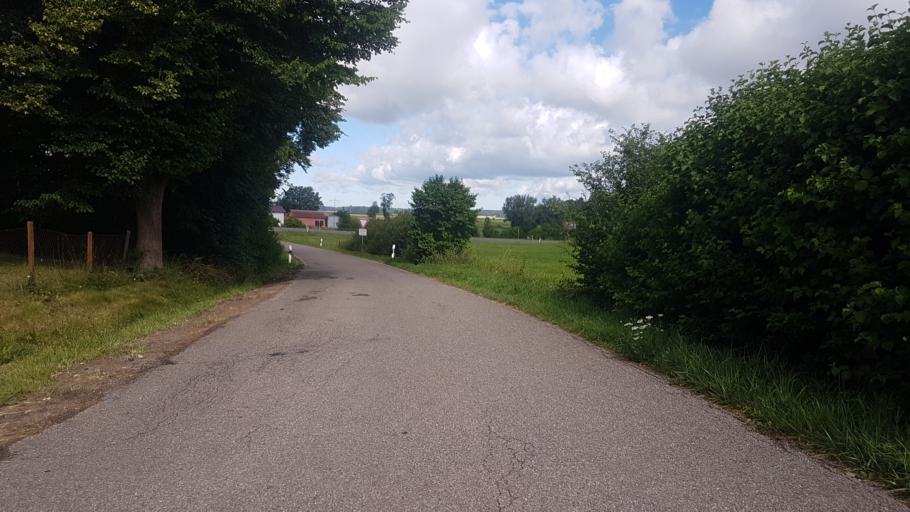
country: DE
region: Bavaria
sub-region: Regierungsbezirk Mittelfranken
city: Ornbau
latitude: 49.1780
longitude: 10.6512
